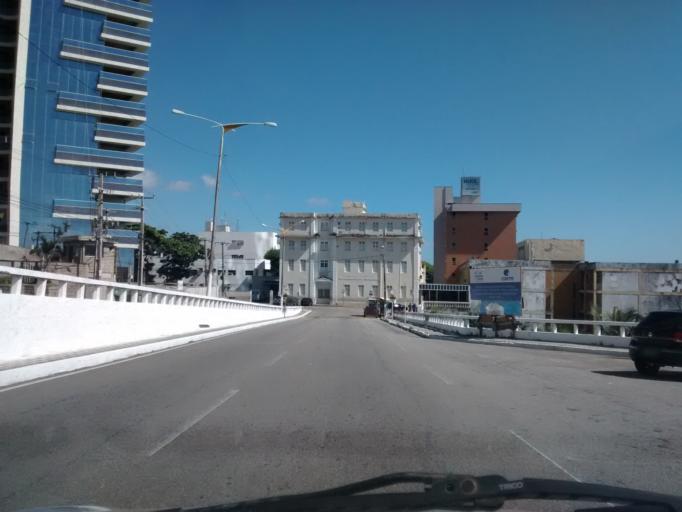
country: BR
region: Rio Grande do Norte
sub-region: Natal
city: Natal
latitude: -5.7814
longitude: -35.1955
